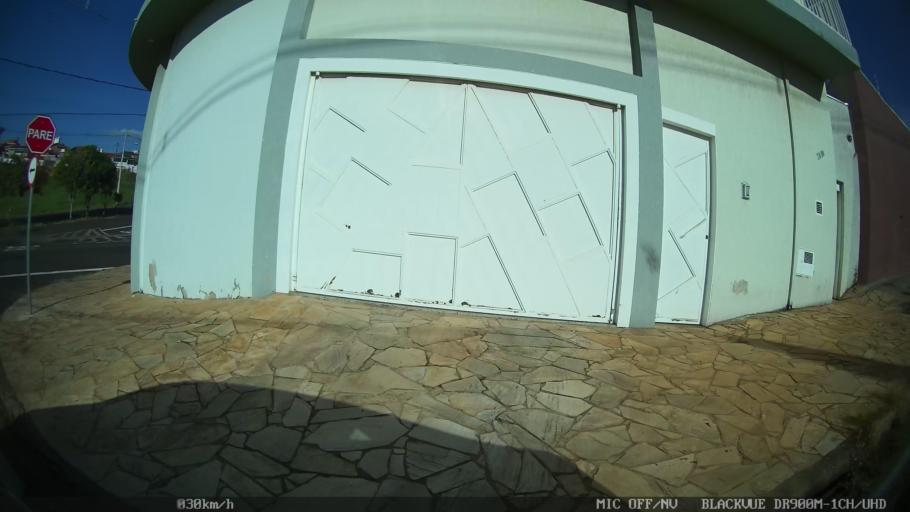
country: BR
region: Sao Paulo
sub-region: Franca
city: Franca
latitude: -20.5235
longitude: -47.4162
